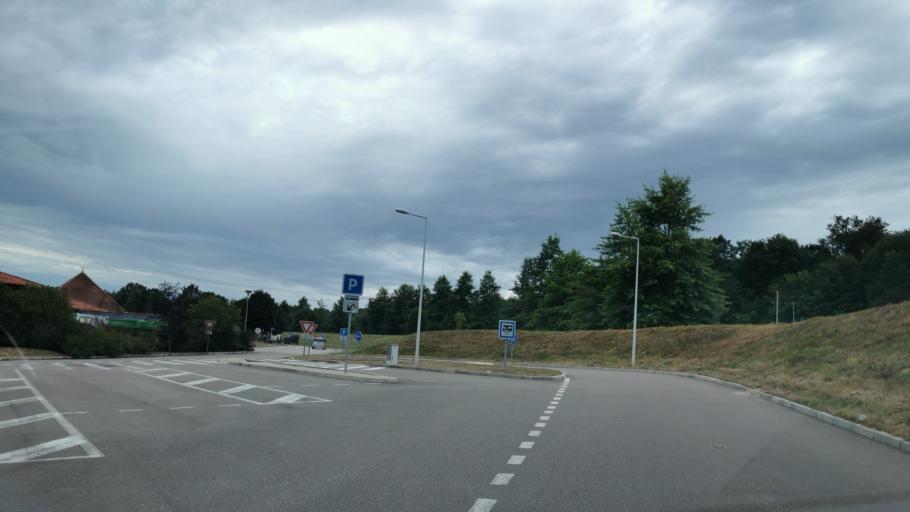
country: FR
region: Bourgogne
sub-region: Departement de Saone-et-Loire
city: Varennes-Saint-Sauveur
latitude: 46.4959
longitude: 5.3104
